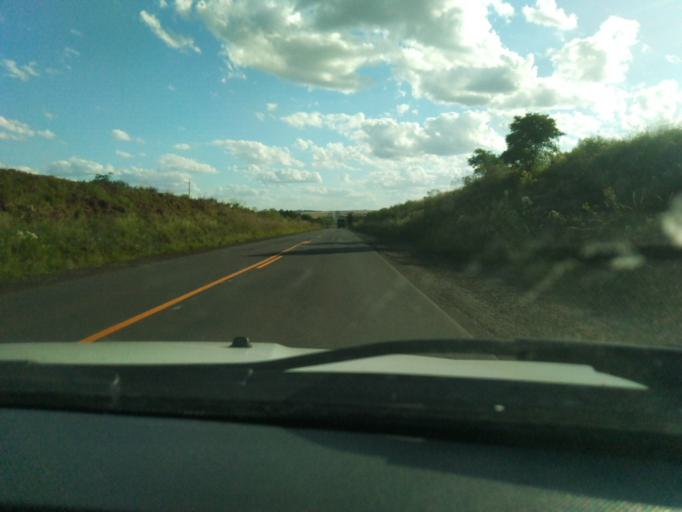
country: AR
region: Corrientes
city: Garruchos
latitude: -28.5530
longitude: -55.5707
